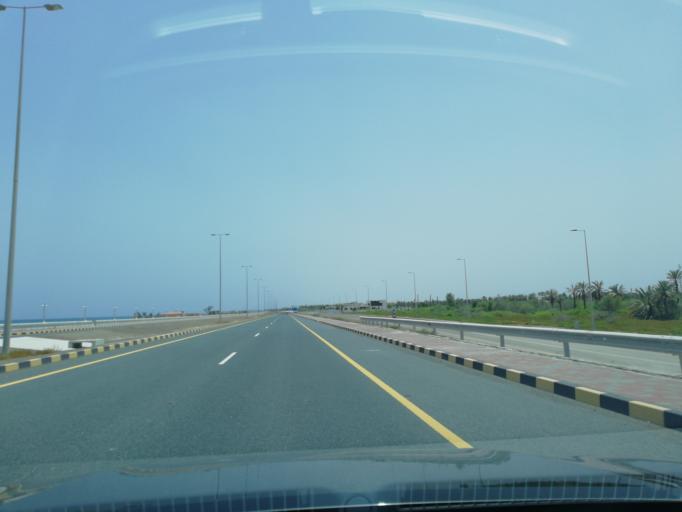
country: OM
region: Al Batinah
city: Shinas
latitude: 24.8195
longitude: 56.4407
